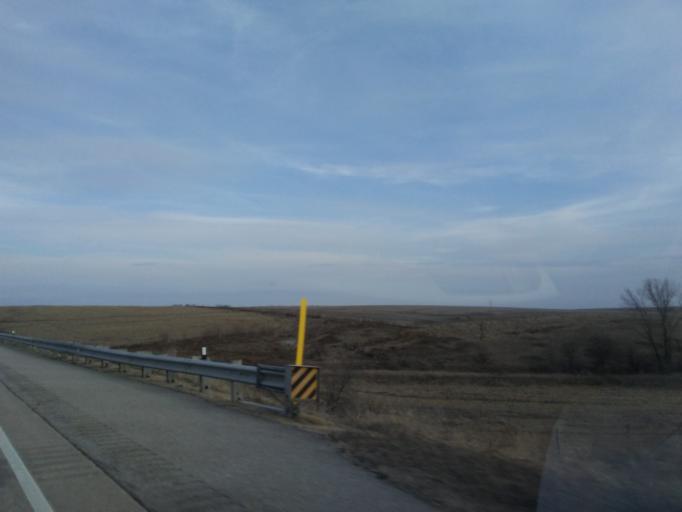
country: US
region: Wisconsin
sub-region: Iowa County
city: Barneveld
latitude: 43.0092
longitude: -89.8600
